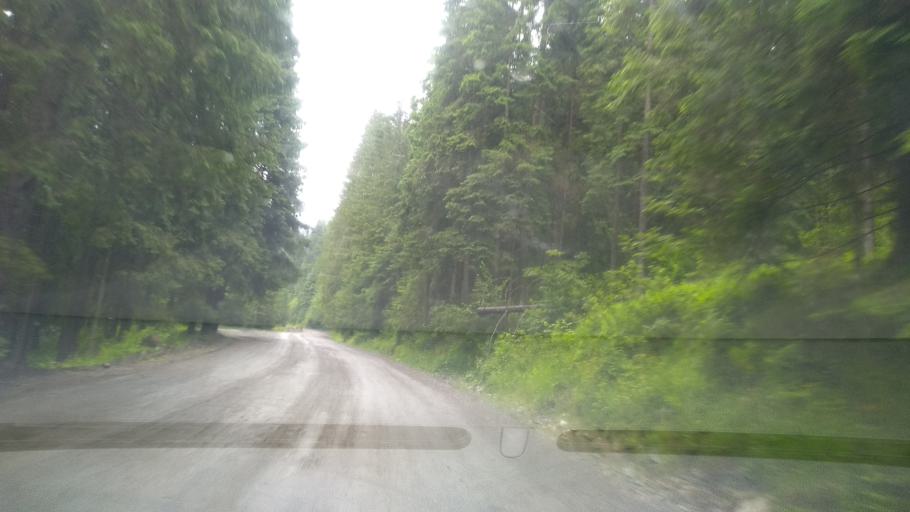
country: RO
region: Hunedoara
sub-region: Oras Petrila
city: Petrila
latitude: 45.4104
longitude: 23.5518
